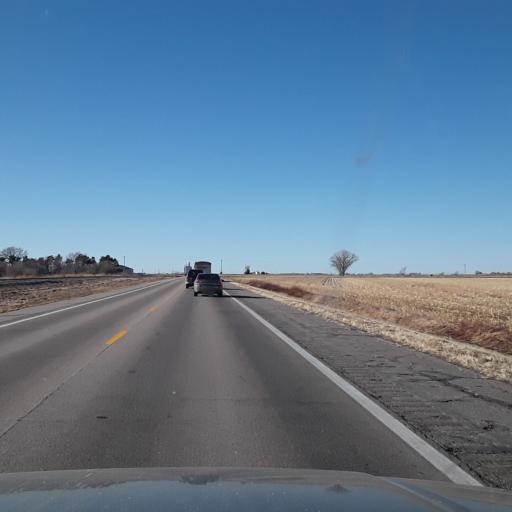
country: US
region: Nebraska
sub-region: Kearney County
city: Minden
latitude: 40.4981
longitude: -98.9840
